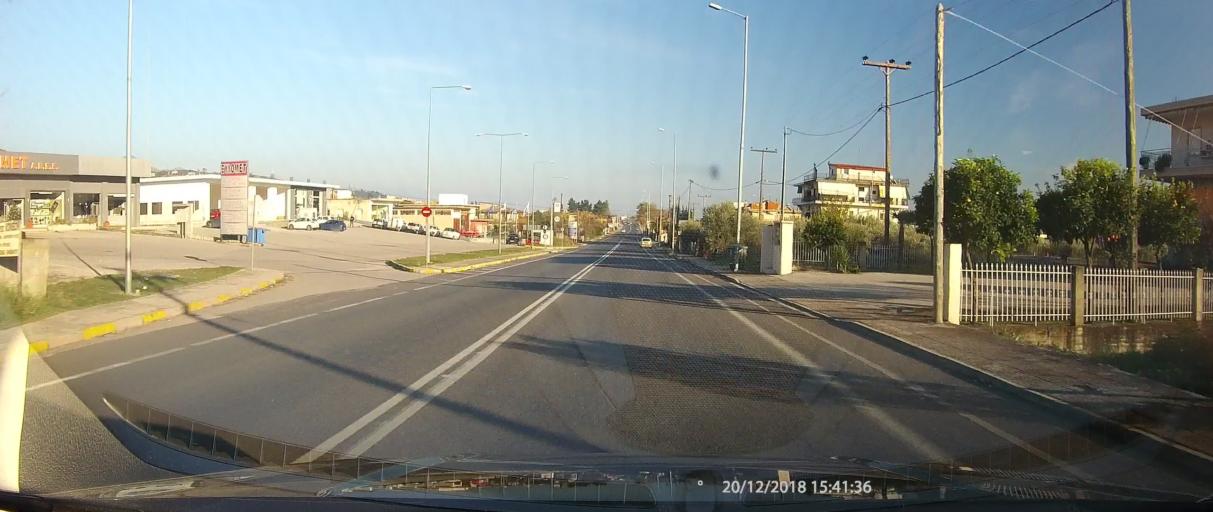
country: GR
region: Central Greece
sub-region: Nomos Fthiotidos
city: Stavros
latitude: 38.8898
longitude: 22.3864
